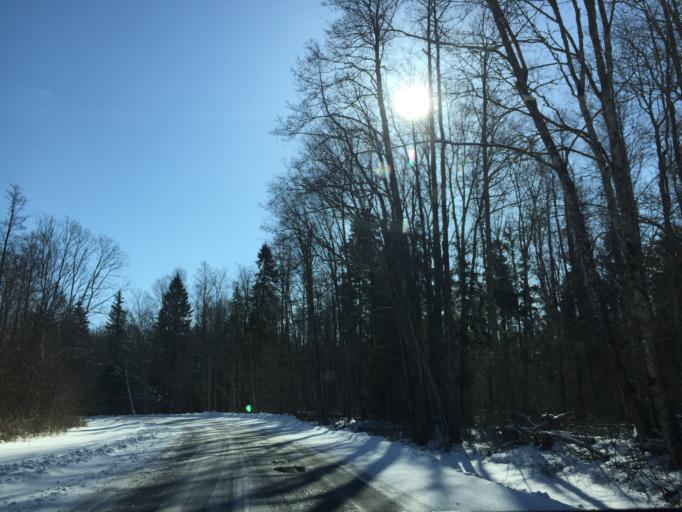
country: LV
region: Salacgrivas
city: Ainazi
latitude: 57.9976
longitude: 24.5355
